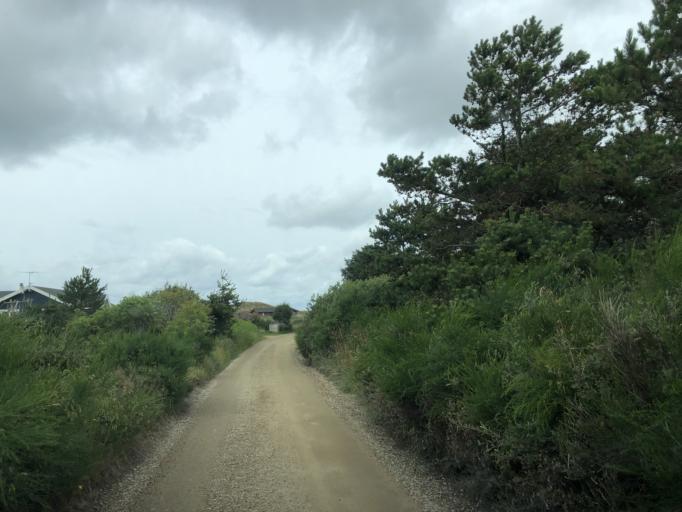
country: DK
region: Central Jutland
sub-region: Ringkobing-Skjern Kommune
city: Hvide Sande
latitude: 55.9233
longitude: 8.1697
